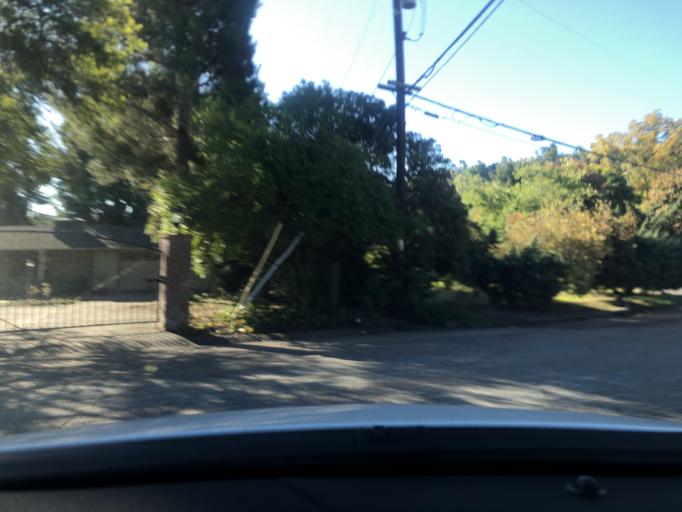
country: US
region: California
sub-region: San Diego County
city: Casa de Oro-Mount Helix
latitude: 32.7641
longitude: -116.9547
